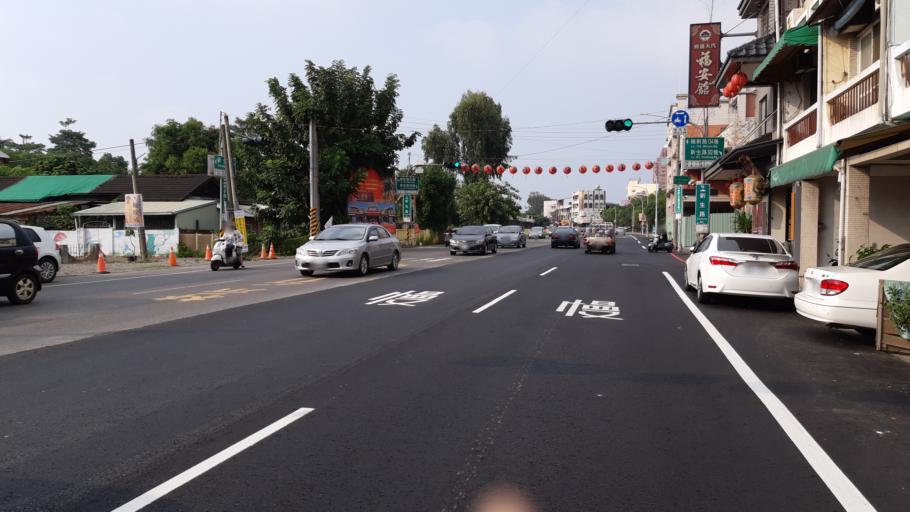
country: TW
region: Taiwan
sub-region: Chiayi
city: Jiayi Shi
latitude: 23.4852
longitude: 120.4607
